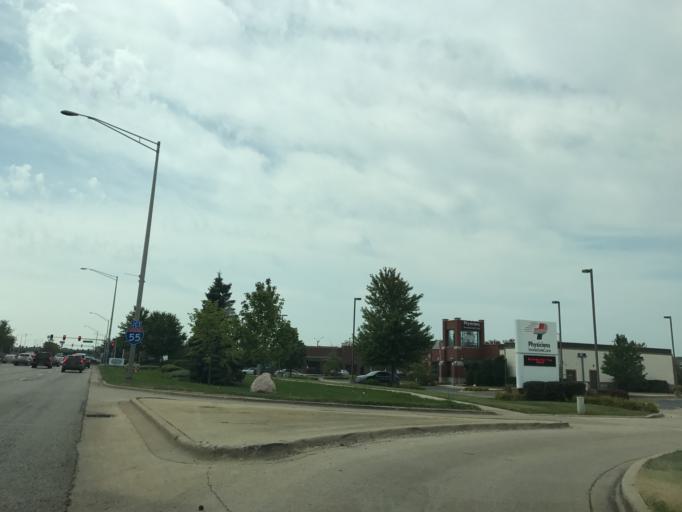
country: US
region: Illinois
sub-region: Will County
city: Bolingbrook
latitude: 41.6893
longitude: -88.0681
